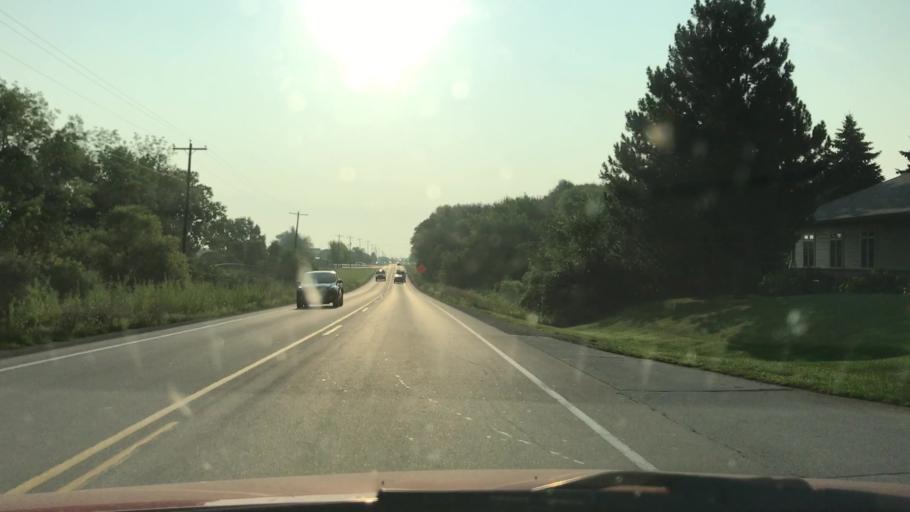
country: US
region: Wisconsin
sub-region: Brown County
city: De Pere
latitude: 44.4298
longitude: -88.1297
